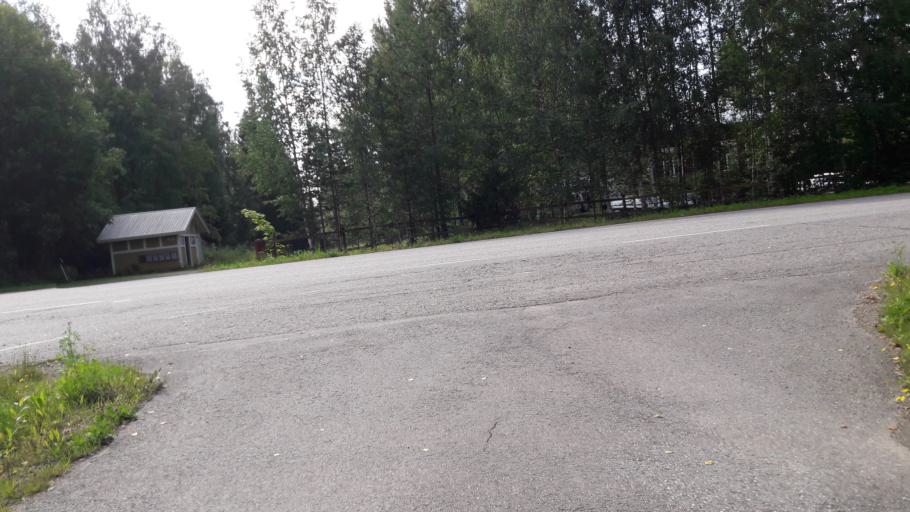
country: FI
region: North Karelia
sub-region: Joensuu
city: Pyhaeselkae
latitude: 62.5195
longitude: 29.8688
